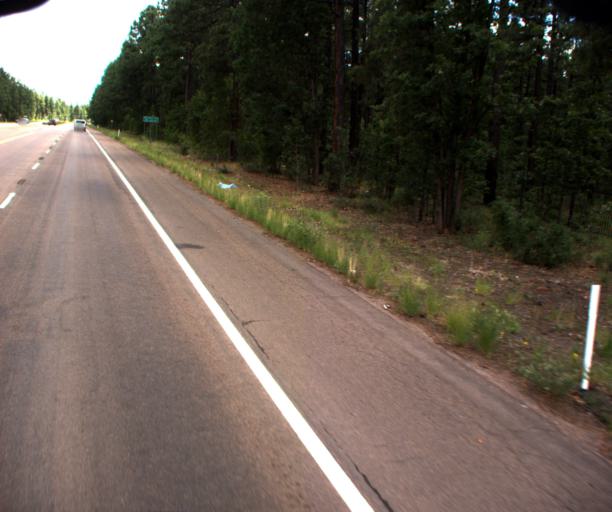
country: US
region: Arizona
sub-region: Navajo County
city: Pinetop-Lakeside
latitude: 34.1065
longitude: -109.9116
